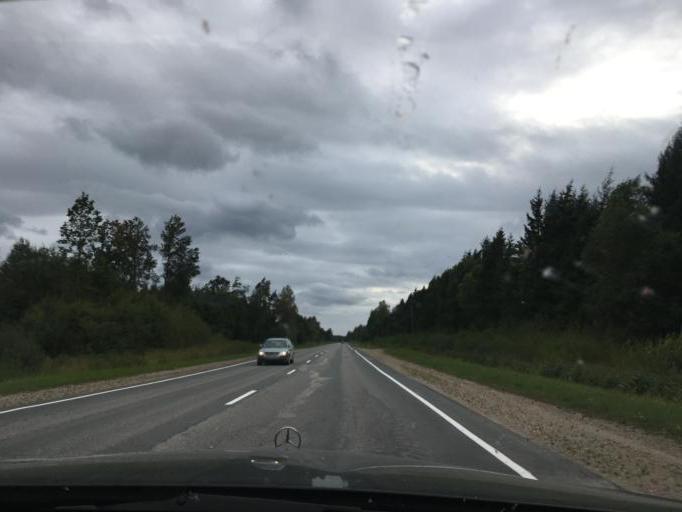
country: LV
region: Smiltene
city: Smiltene
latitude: 57.3552
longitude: 25.8911
